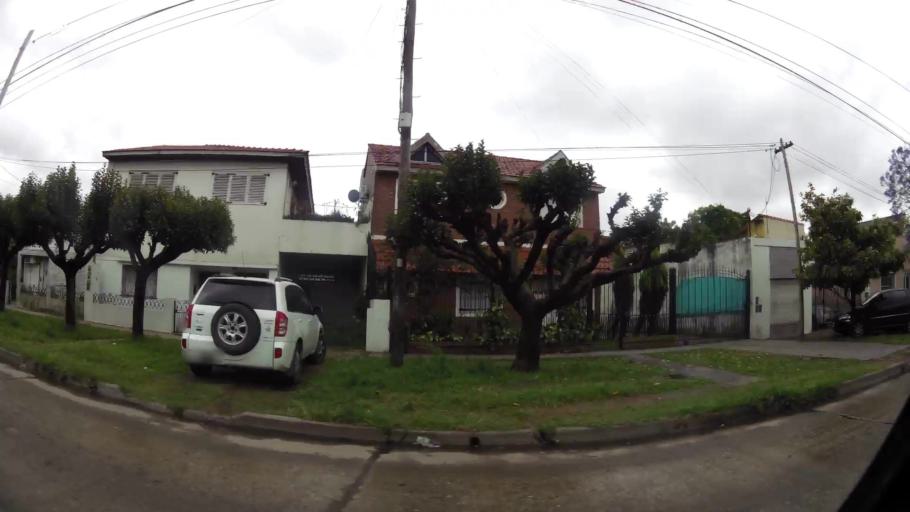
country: AR
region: Buenos Aires
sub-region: Partido de Lomas de Zamora
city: Lomas de Zamora
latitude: -34.7417
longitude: -58.3726
